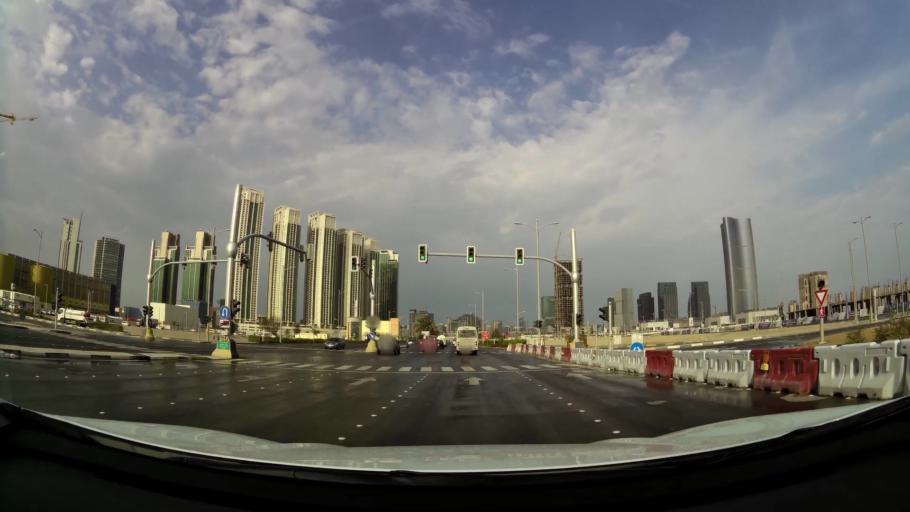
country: AE
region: Abu Dhabi
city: Abu Dhabi
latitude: 24.4926
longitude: 54.4012
